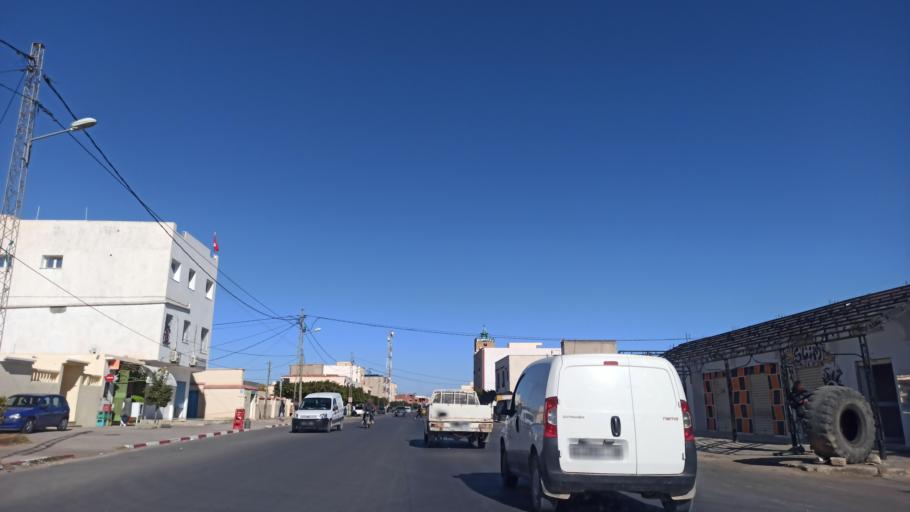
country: TN
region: Sidi Bu Zayd
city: Bi'r al Hufayy
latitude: 34.9245
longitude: 9.1901
